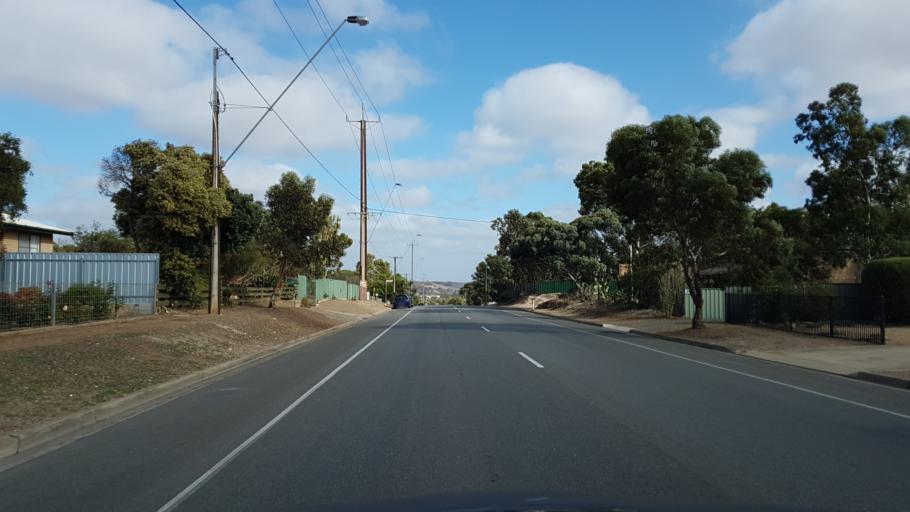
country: AU
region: South Australia
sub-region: Murray Bridge
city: Murray Bridge
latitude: -35.1212
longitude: 139.2526
